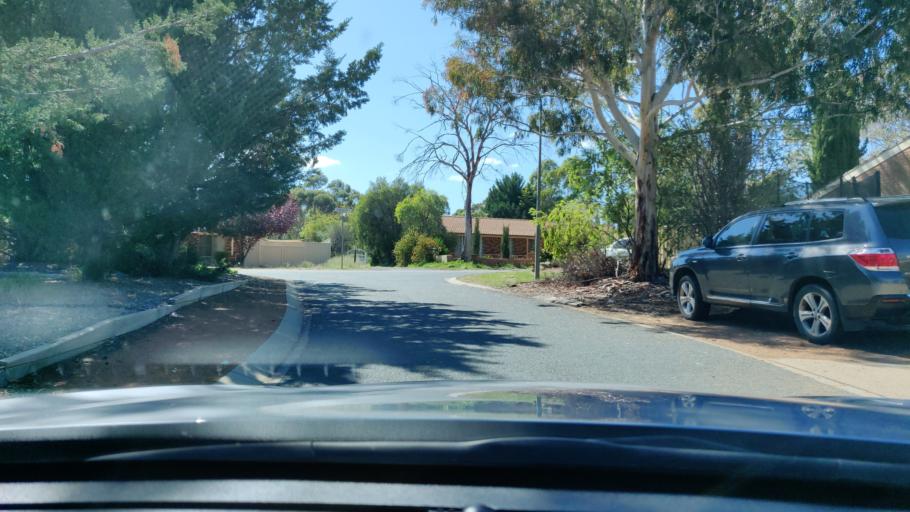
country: AU
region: Australian Capital Territory
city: Macarthur
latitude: -35.4402
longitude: 149.0962
